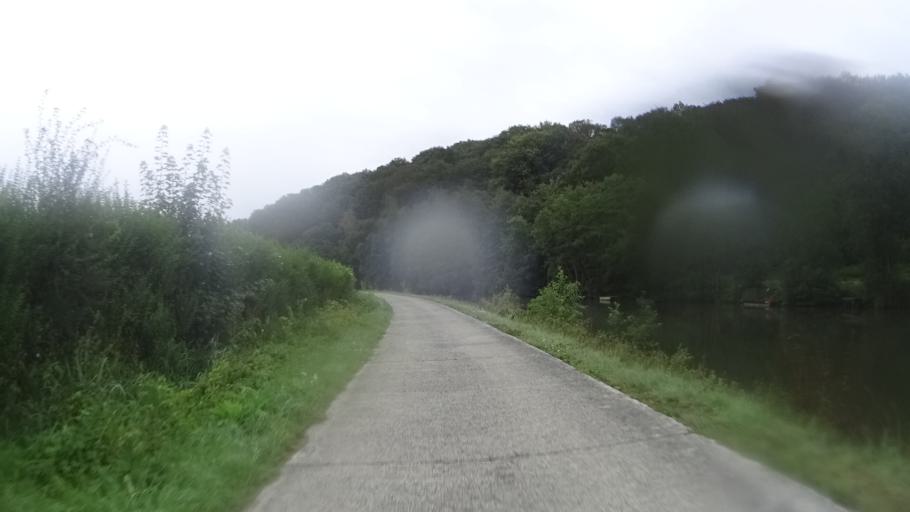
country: BE
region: Wallonia
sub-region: Province du Hainaut
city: Lobbes
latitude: 50.3461
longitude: 4.2574
